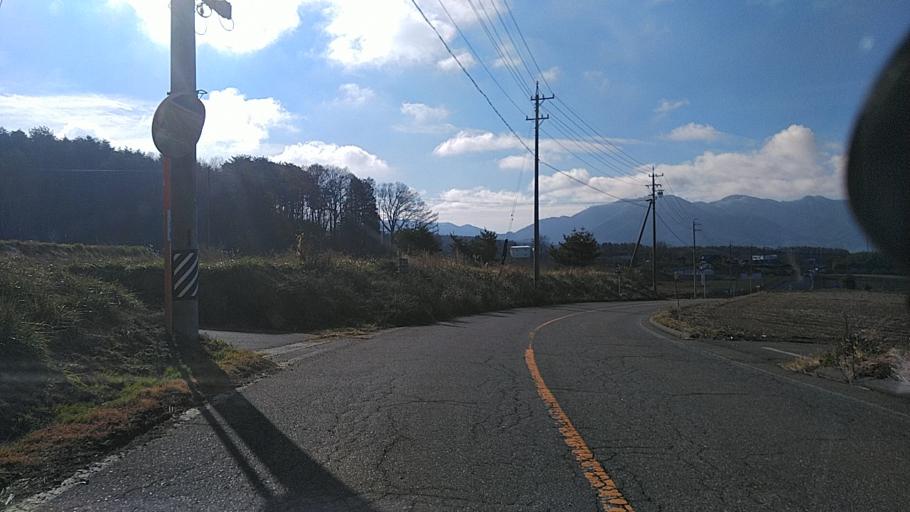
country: JP
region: Nagano
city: Shiojiri
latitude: 36.1331
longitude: 137.9878
